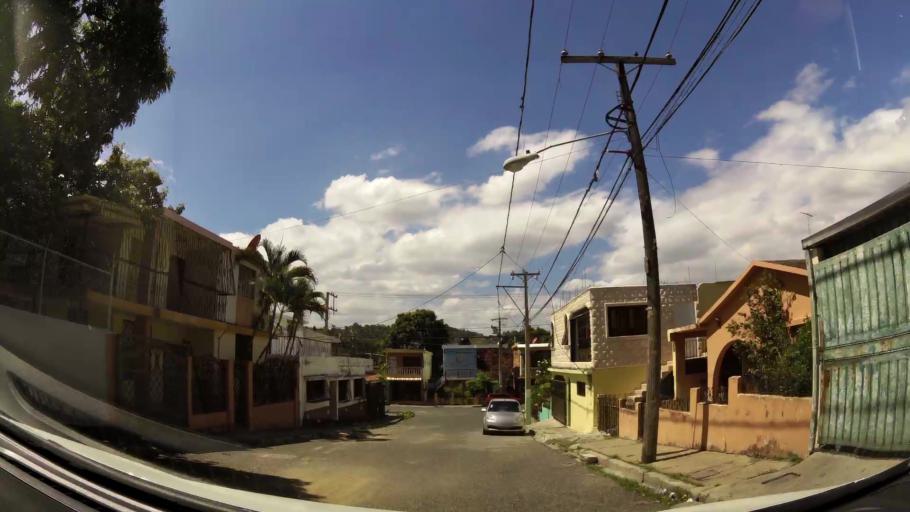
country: DO
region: San Cristobal
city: San Cristobal
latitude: 18.4104
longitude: -70.1078
